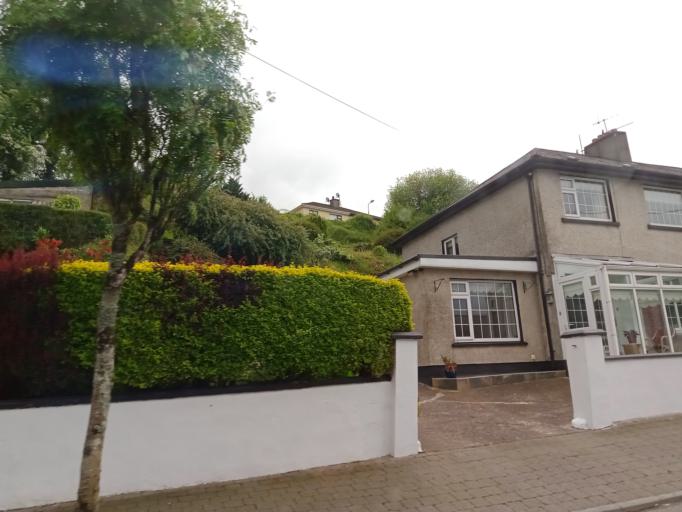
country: IE
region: Munster
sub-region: County Cork
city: Bandon
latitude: 51.7435
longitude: -8.7436
